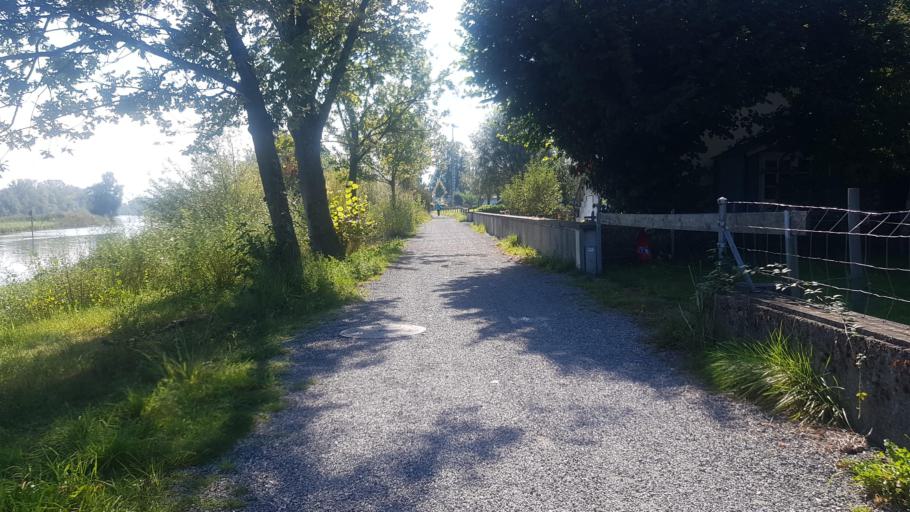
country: CH
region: Saint Gallen
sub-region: Wahlkreis Rheintal
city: Rheineck
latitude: 47.4944
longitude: 9.5627
